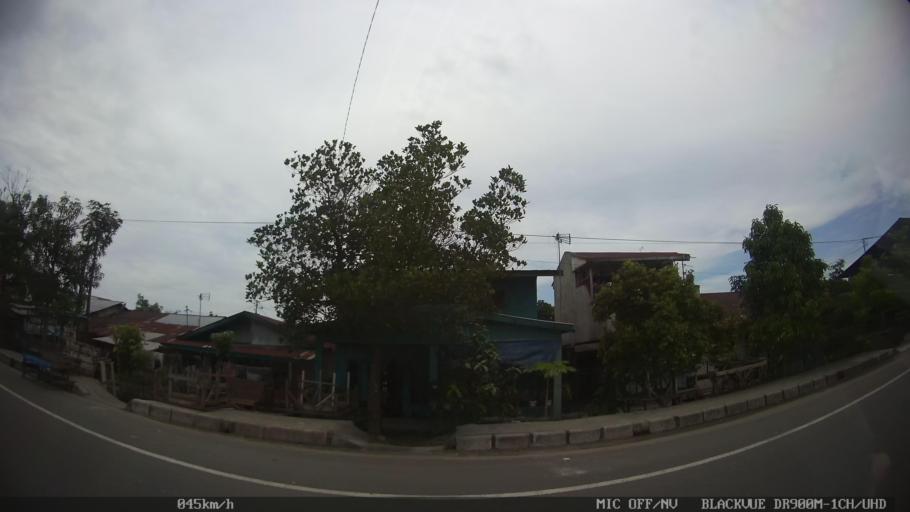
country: ID
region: North Sumatra
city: Sunggal
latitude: 3.6020
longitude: 98.5752
